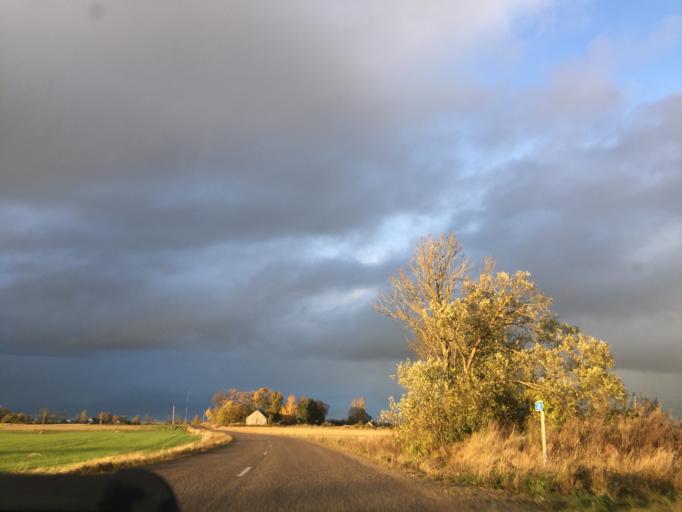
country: LV
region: Talsu Rajons
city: Sabile
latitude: 56.9319
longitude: 22.3972
